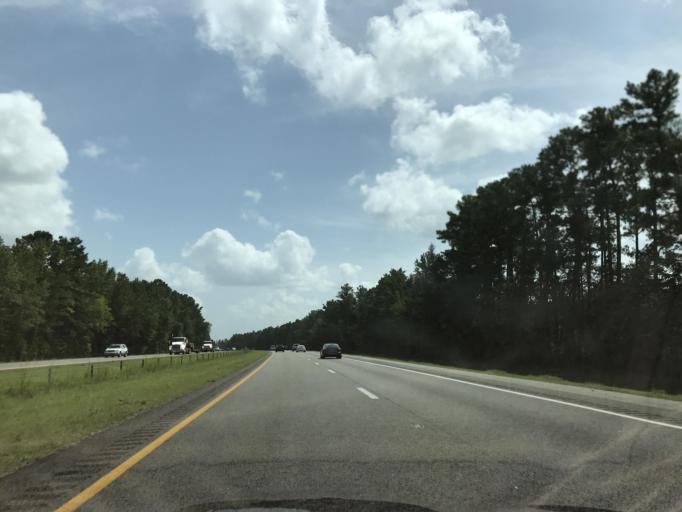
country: US
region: North Carolina
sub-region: Pender County
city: Burgaw
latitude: 34.5335
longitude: -77.8933
